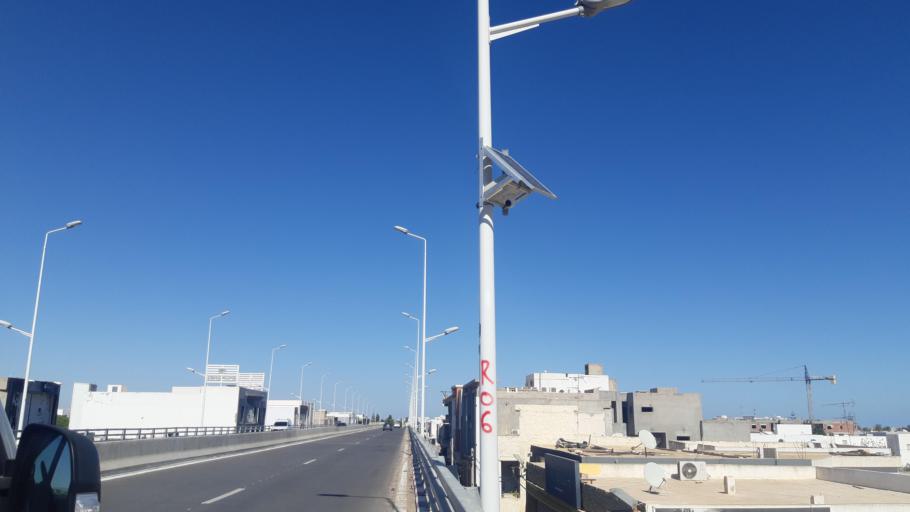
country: TN
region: Safaqis
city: Sfax
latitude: 34.7640
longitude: 10.7429
